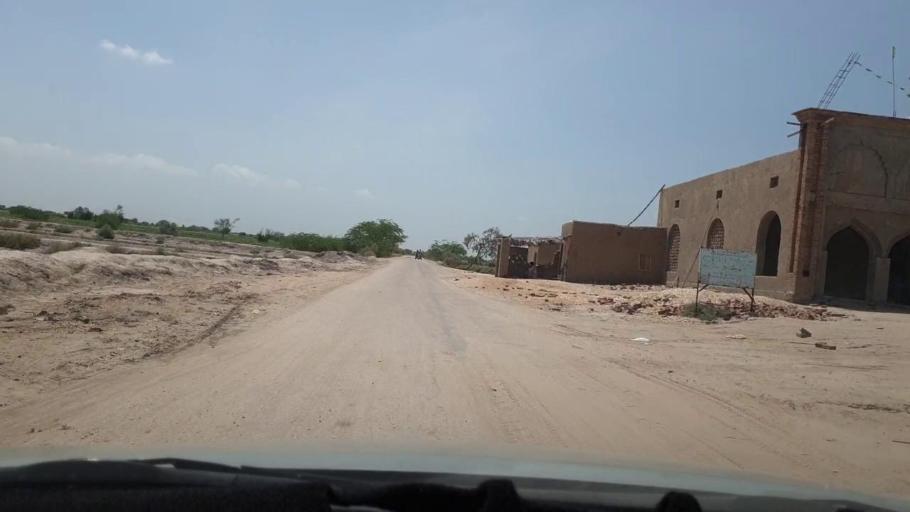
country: PK
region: Sindh
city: Pano Aqil
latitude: 27.6634
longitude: 69.1605
